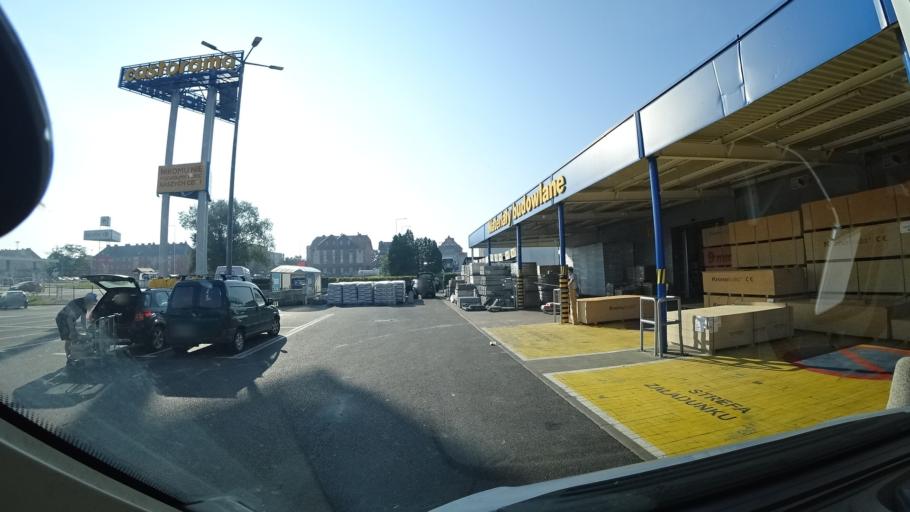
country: PL
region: Opole Voivodeship
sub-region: Powiat kedzierzynsko-kozielski
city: Kedzierzyn-Kozle
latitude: 50.3410
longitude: 18.1925
